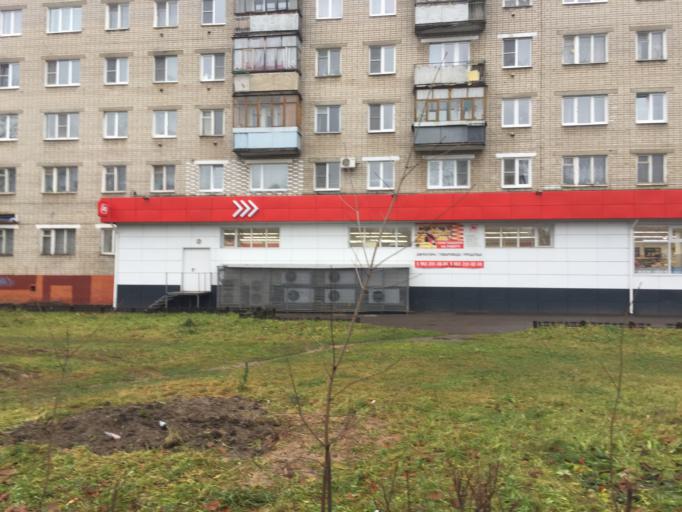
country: RU
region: Jaroslavl
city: Yaroslavl
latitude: 57.7135
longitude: 39.7737
